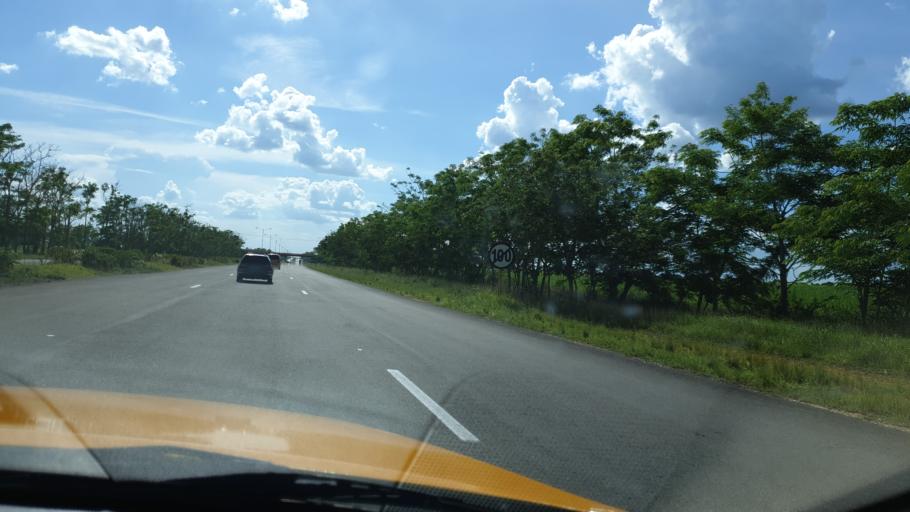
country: CU
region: Cienfuegos
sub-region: Municipio de Aguada de Pasajeros
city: Aguada de Pasajeros
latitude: 22.4026
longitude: -80.8576
